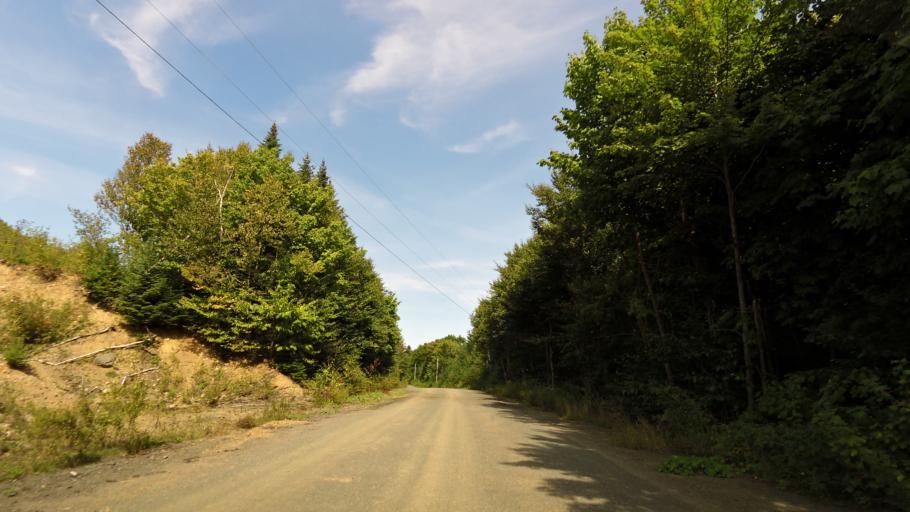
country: CA
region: New Brunswick
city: Hampton
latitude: 45.5714
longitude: -65.8327
